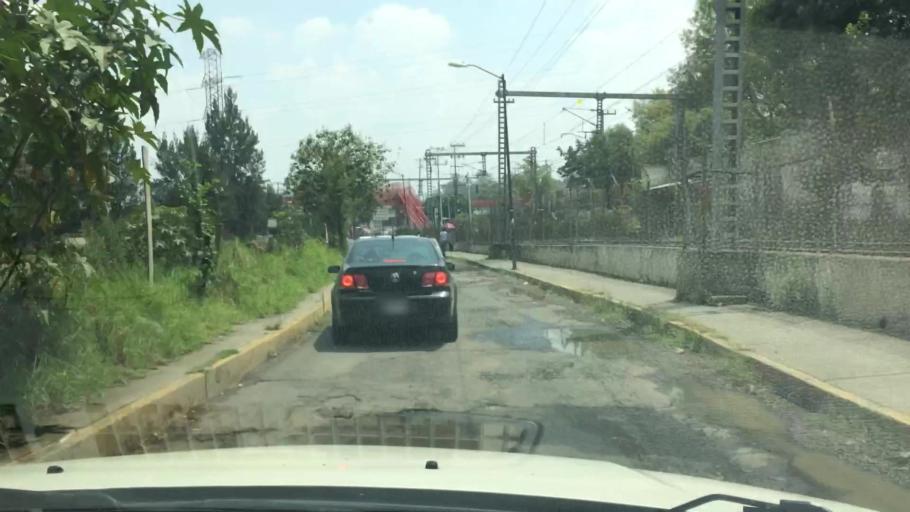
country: MX
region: Mexico City
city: Xochimilco
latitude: 19.2698
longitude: -99.1285
